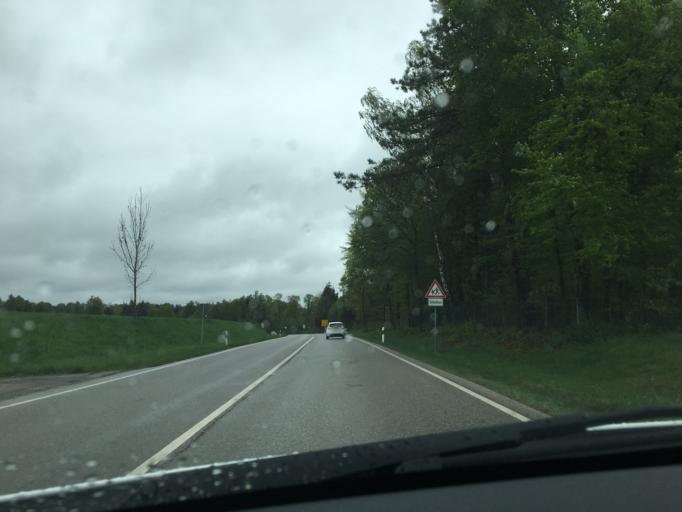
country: DE
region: Bavaria
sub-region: Upper Bavaria
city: Schaftlarn
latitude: 47.9699
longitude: 11.4493
